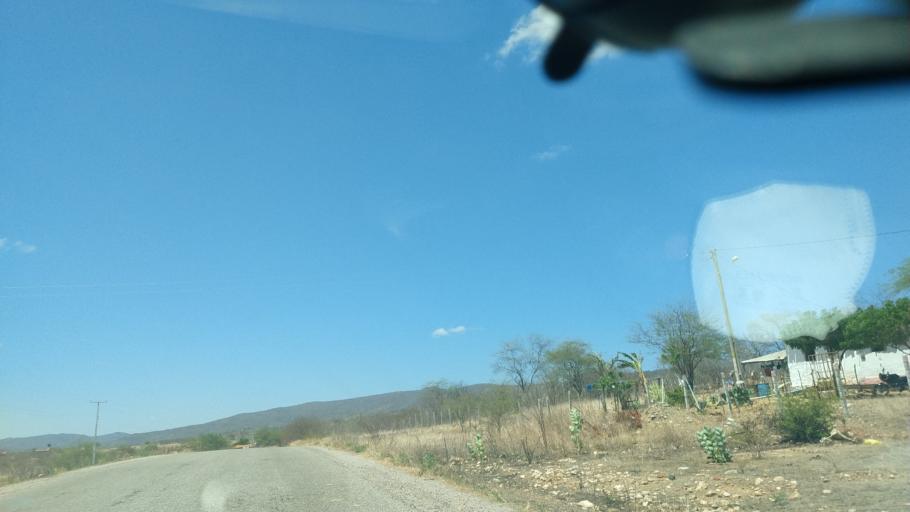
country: BR
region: Rio Grande do Norte
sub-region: Sao Tome
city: Sao Tome
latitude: -5.9769
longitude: -36.1474
